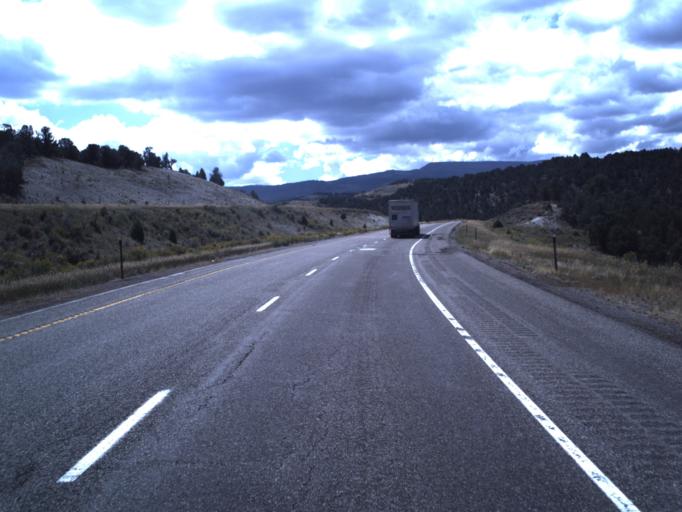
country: US
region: Utah
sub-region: Sevier County
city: Salina
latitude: 38.8655
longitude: -111.5522
